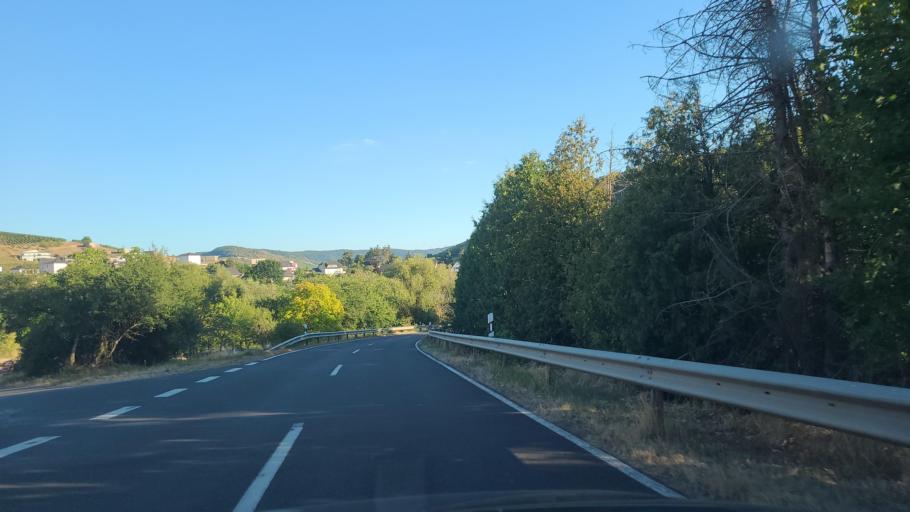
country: DE
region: Rheinland-Pfalz
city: Klusserath
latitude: 49.8499
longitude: 6.8419
